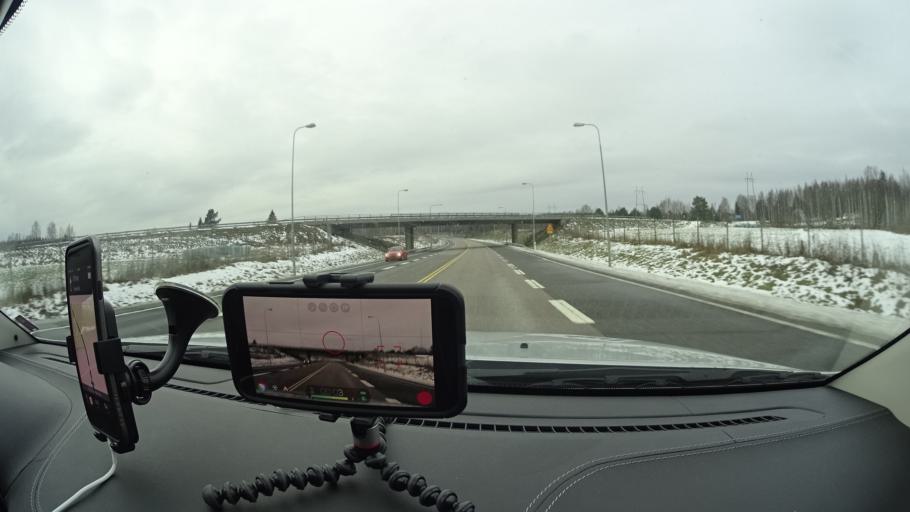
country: FI
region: Paijanne Tavastia
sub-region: Lahti
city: Heinola
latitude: 61.2945
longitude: 26.0725
